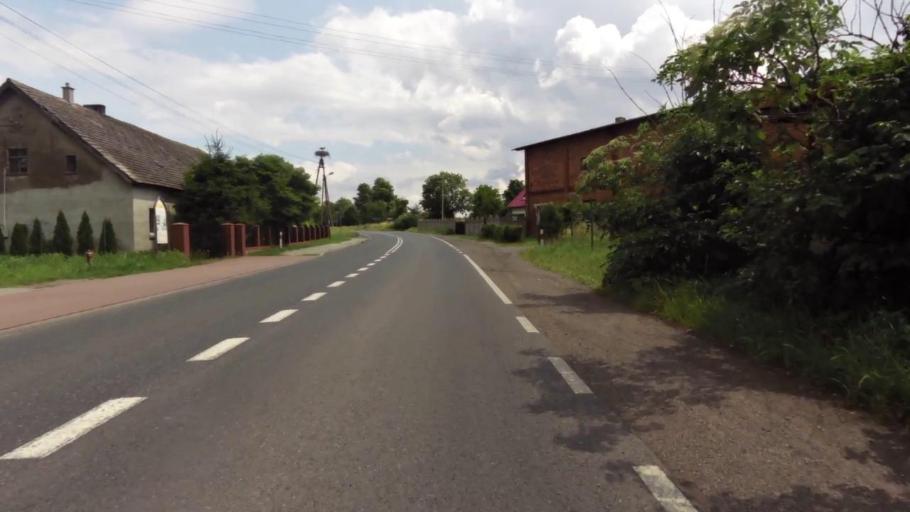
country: PL
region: West Pomeranian Voivodeship
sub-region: Powiat pyrzycki
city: Lipiany
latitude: 52.9991
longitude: 15.0316
